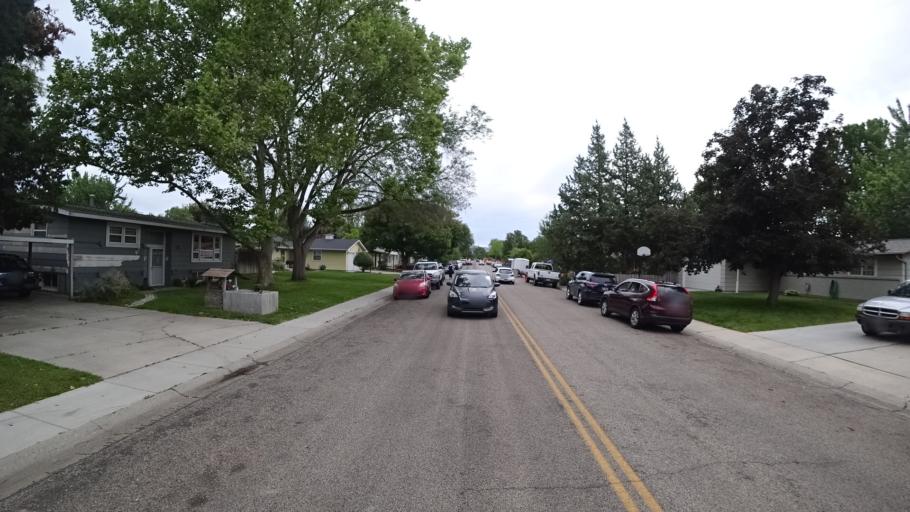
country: US
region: Idaho
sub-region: Ada County
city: Boise
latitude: 43.5772
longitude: -116.2068
